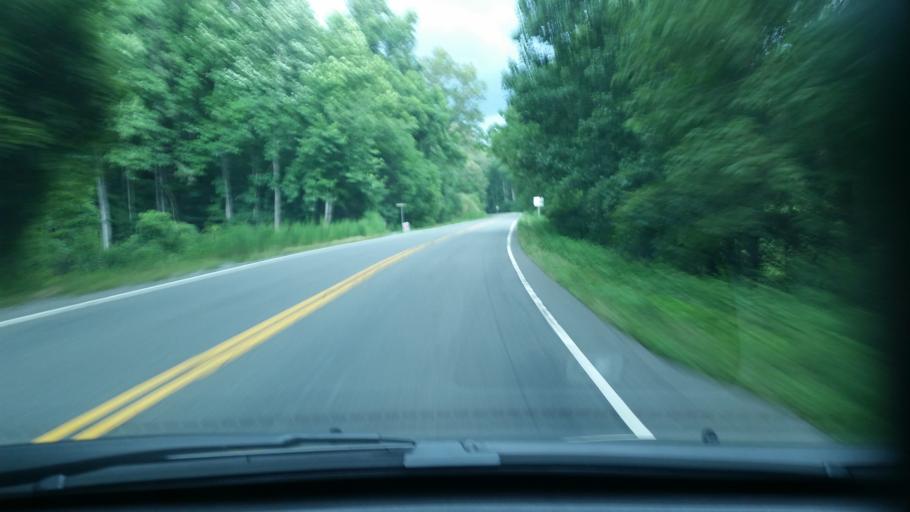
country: US
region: Virginia
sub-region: Nelson County
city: Nellysford
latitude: 37.8551
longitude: -78.8156
